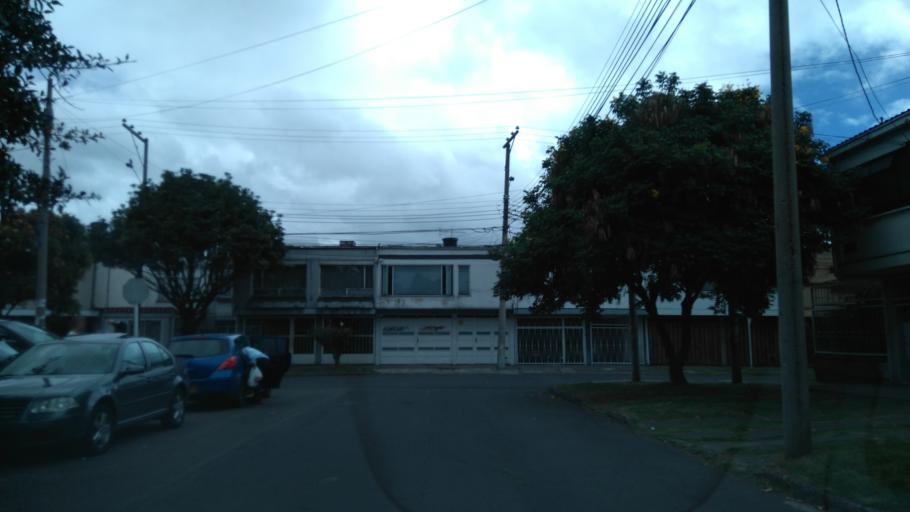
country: CO
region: Bogota D.C.
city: Barrio San Luis
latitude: 4.6734
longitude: -74.0640
